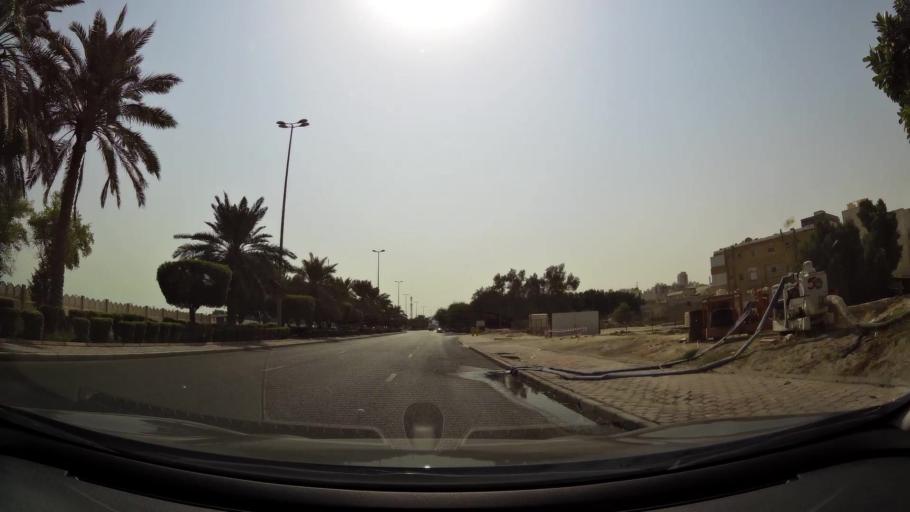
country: KW
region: Al Ahmadi
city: Al Fintas
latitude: 29.1744
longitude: 48.1224
